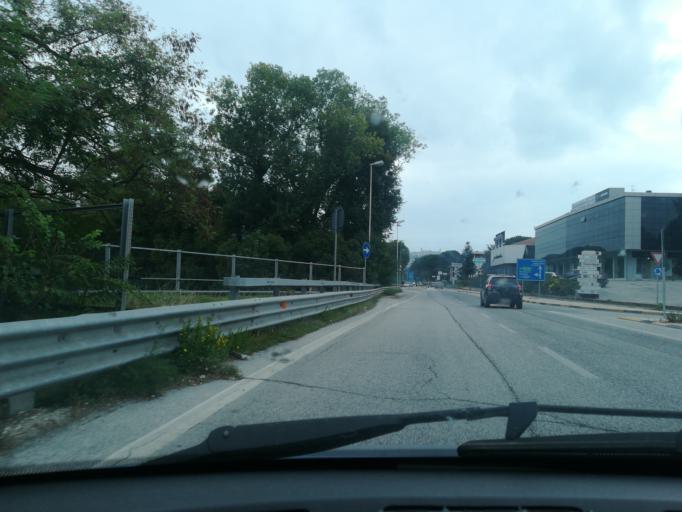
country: IT
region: The Marches
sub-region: Provincia di Macerata
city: Zona Industriale
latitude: 43.2661
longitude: 13.4885
